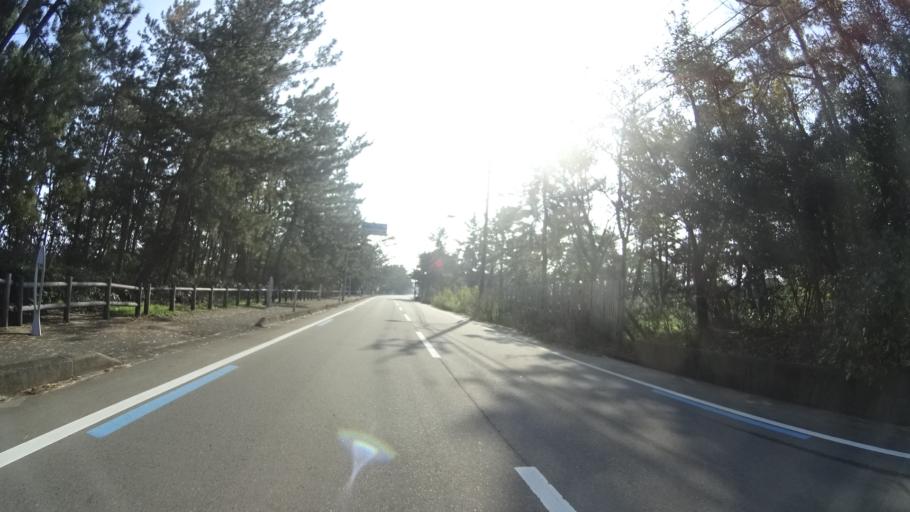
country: JP
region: Toyama
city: Himi
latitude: 36.8353
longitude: 137.0075
